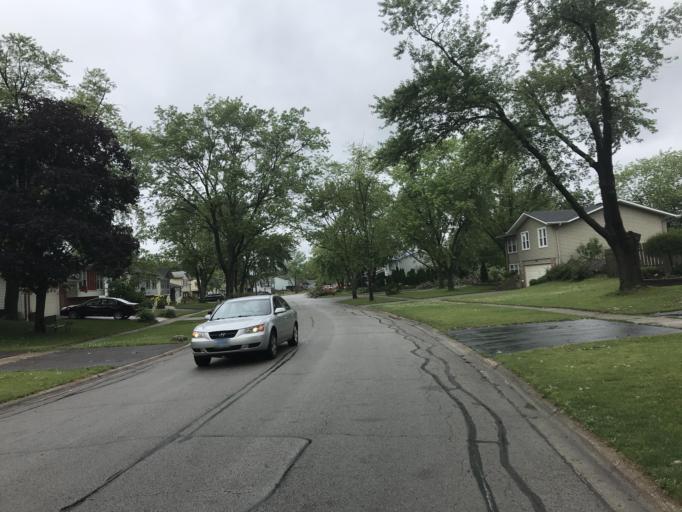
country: US
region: Illinois
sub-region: DuPage County
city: Woodridge
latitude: 41.7416
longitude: -88.0542
